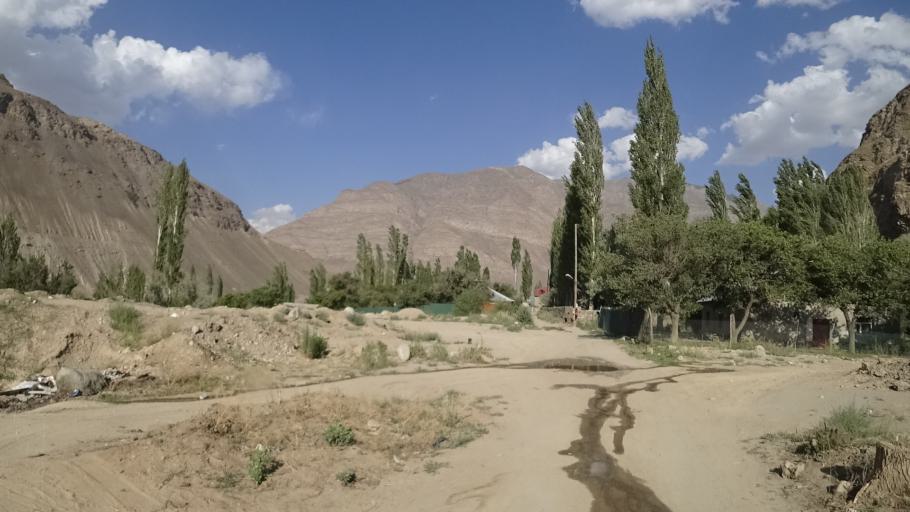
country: TJ
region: Gorno-Badakhshan
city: Khorugh
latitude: 37.4872
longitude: 71.5606
